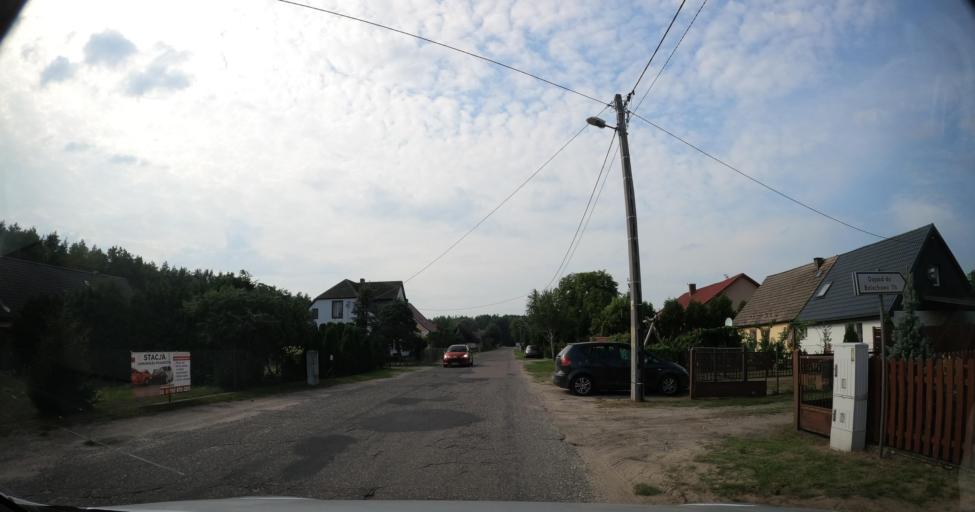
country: PL
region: West Pomeranian Voivodeship
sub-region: Powiat goleniowski
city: Goleniow
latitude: 53.5060
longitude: 14.8709
